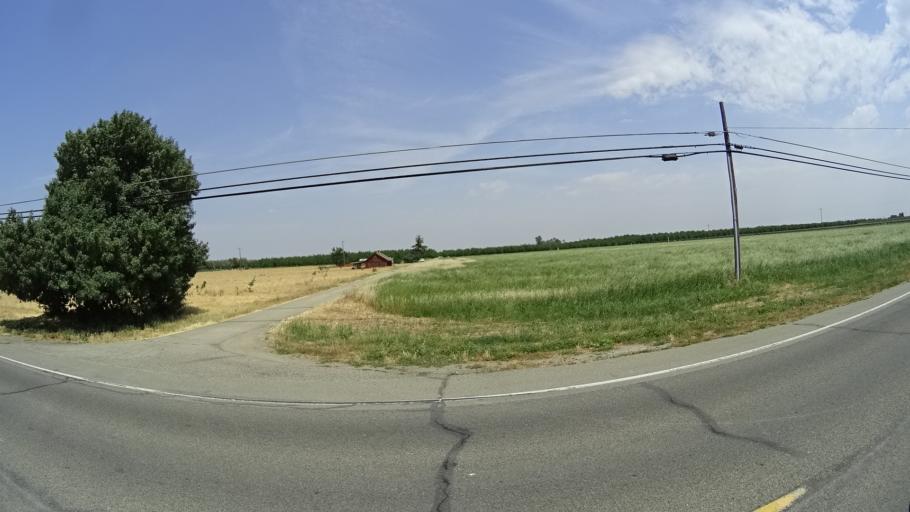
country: US
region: California
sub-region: Kings County
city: Armona
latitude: 36.3280
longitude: -119.7023
